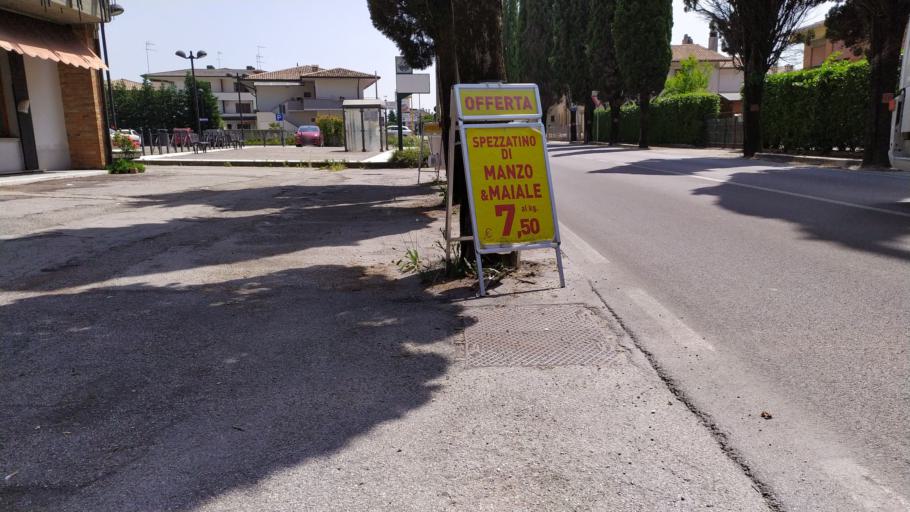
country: IT
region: Veneto
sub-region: Provincia di Treviso
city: Bigolino
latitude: 45.8568
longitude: 12.0246
